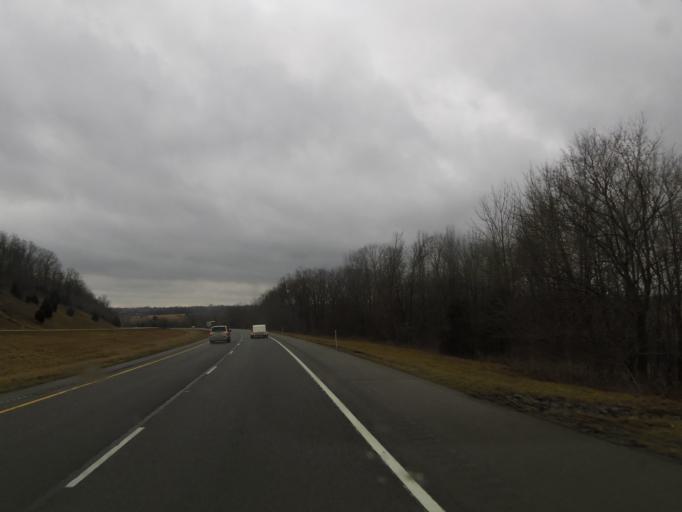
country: US
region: Illinois
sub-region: Johnson County
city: Vienna
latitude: 37.3436
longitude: -88.7870
